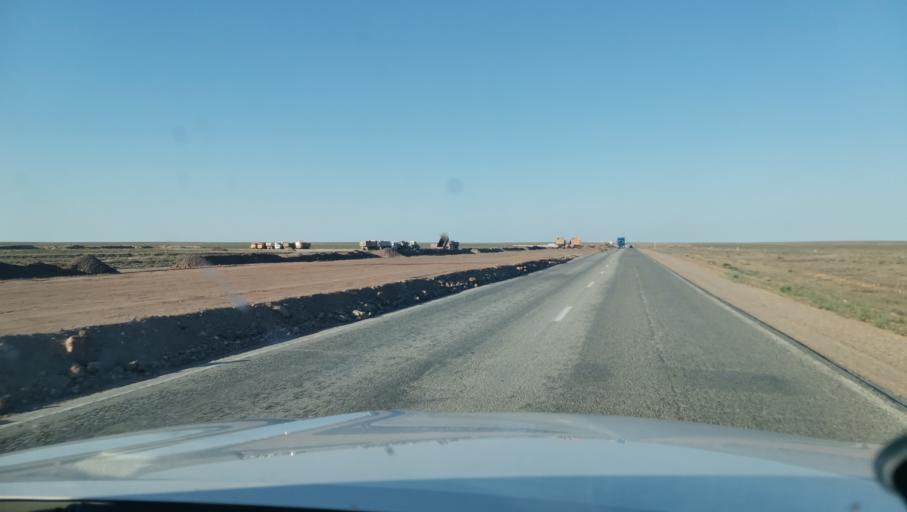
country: KZ
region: Qaraghandy
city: Saryshaghan
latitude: 46.4140
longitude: 73.9086
